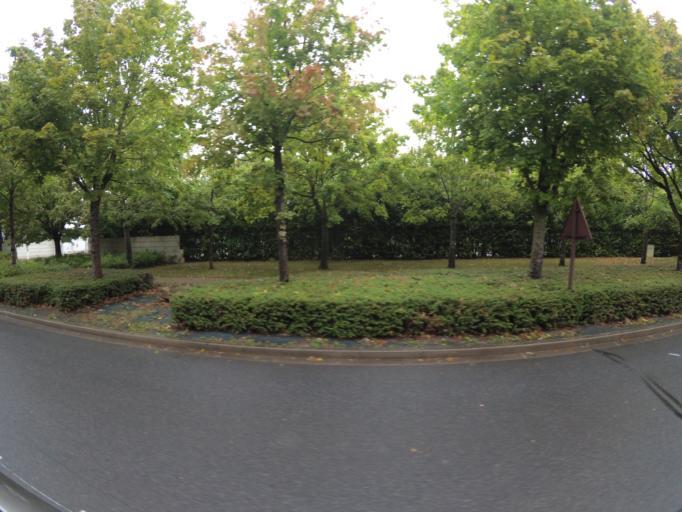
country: FR
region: Ile-de-France
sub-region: Departement de Seine-et-Marne
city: Ferrieres-en-Brie
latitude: 48.8312
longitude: 2.7275
